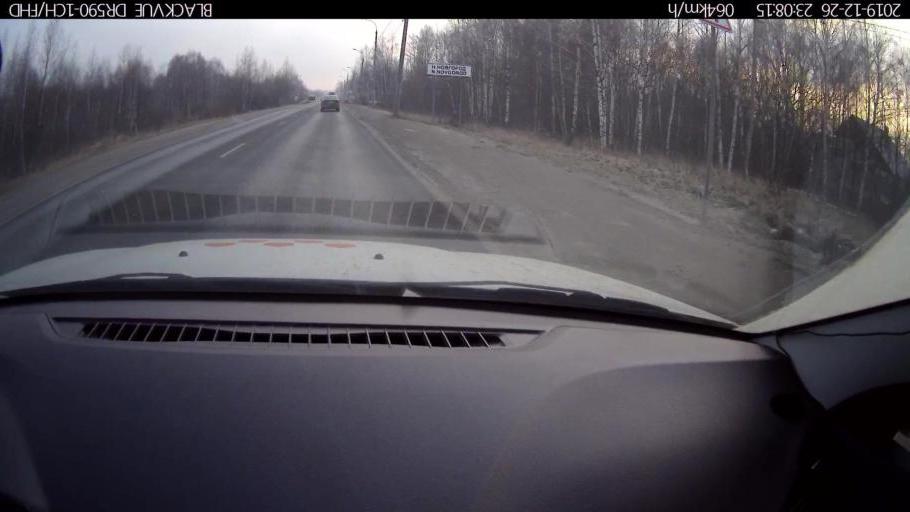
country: RU
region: Nizjnij Novgorod
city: Gorbatovka
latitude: 56.2153
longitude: 43.7593
